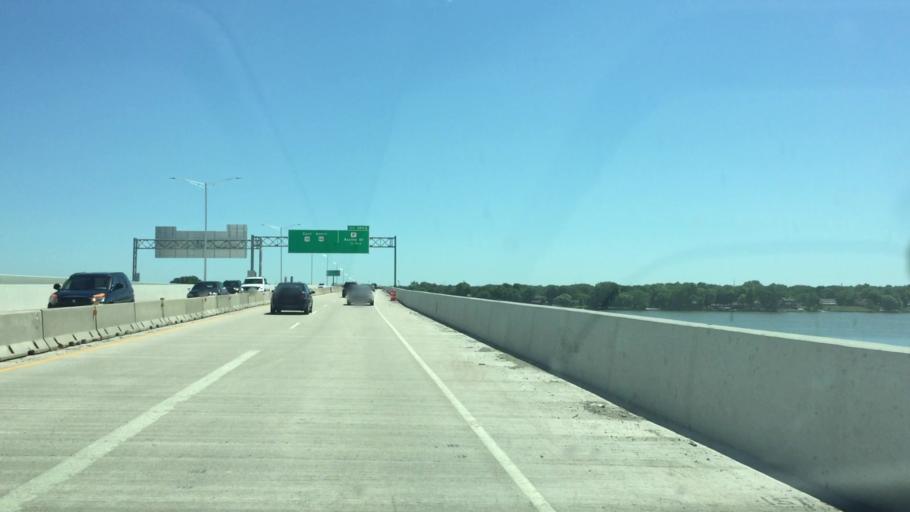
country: US
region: Wisconsin
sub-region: Winnebago County
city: Menasha
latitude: 44.2180
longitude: -88.4660
